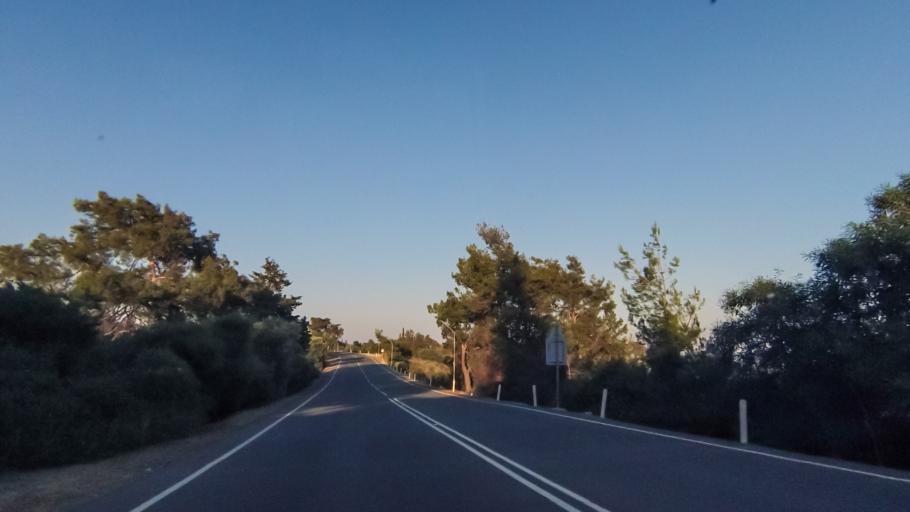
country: CY
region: Limassol
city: Sotira
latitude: 34.6743
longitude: 32.8417
